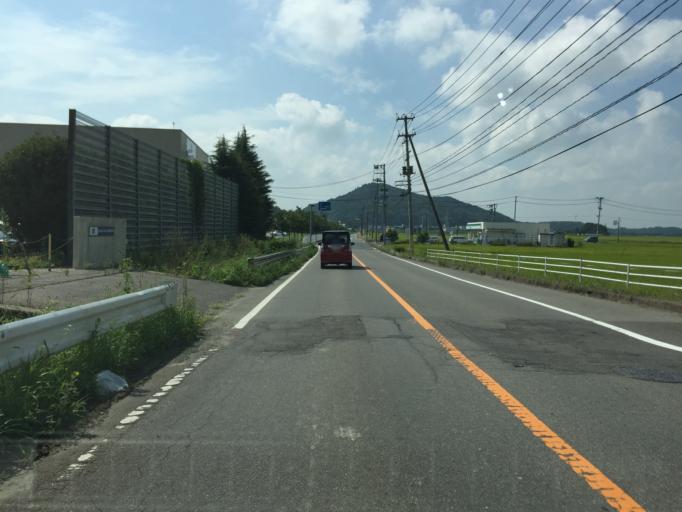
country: JP
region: Fukushima
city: Motomiya
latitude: 37.4902
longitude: 140.4009
